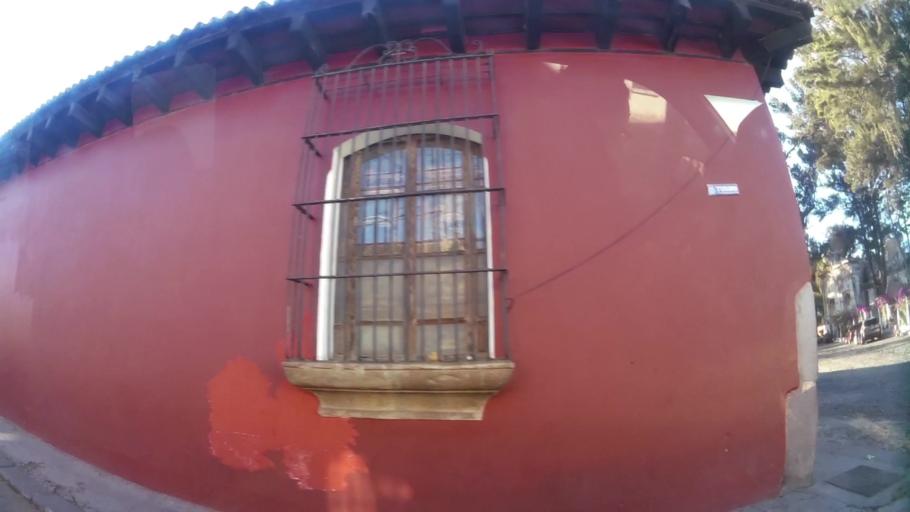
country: GT
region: Sacatepequez
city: Antigua Guatemala
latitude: 14.5638
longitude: -90.7363
